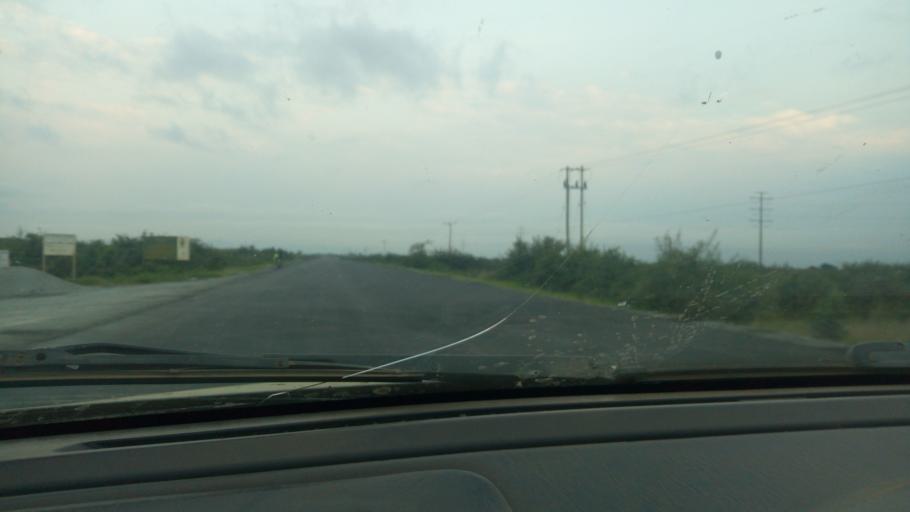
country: UG
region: Western Region
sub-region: Rubirizi District
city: Rubirizi
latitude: -0.1483
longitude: 30.0662
